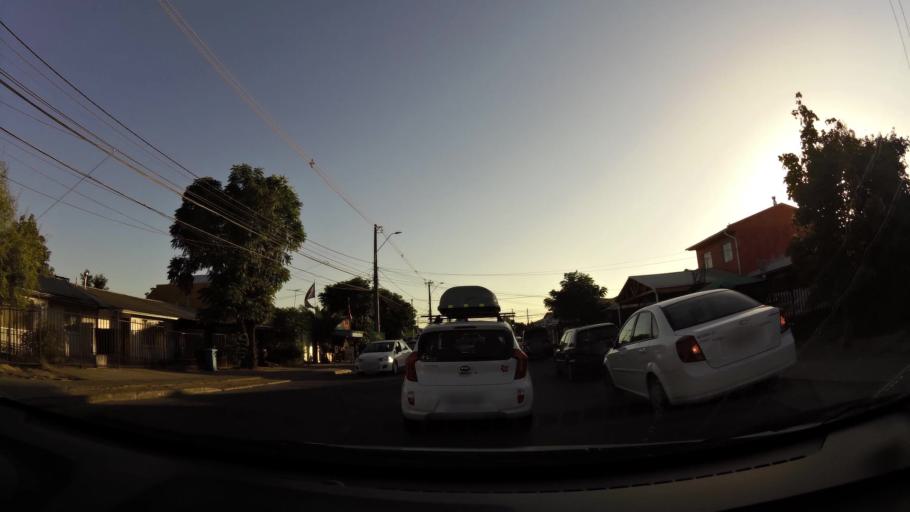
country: CL
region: Maule
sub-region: Provincia de Talca
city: Talca
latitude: -35.4461
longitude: -71.6810
